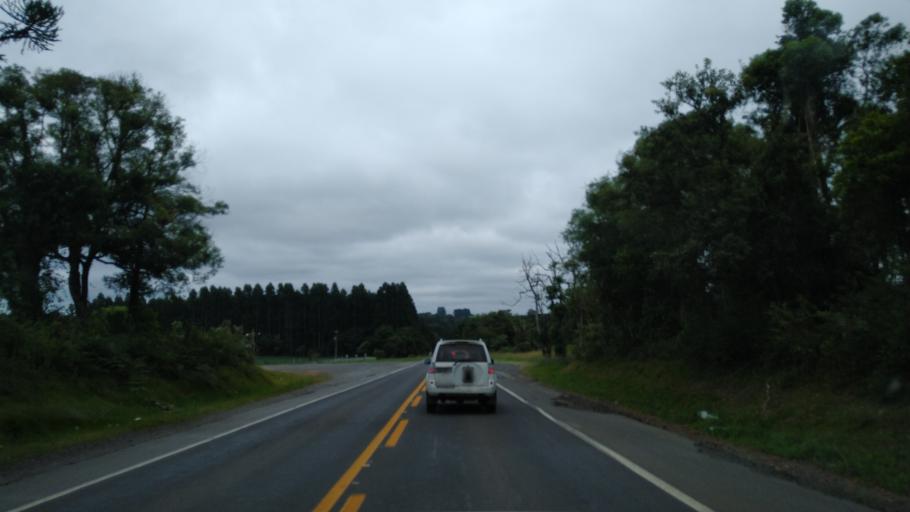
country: BR
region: Santa Catarina
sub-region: Tres Barras
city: Tres Barras
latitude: -26.1815
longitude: -50.1996
